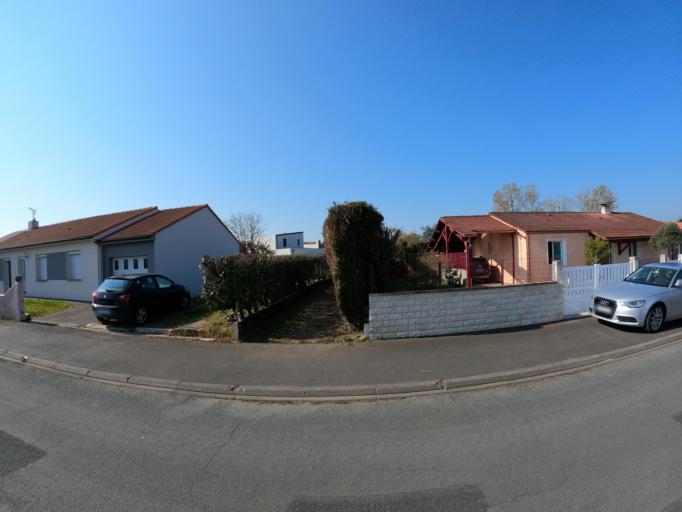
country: FR
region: Pays de la Loire
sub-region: Departement de la Loire-Atlantique
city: Aigrefeuille-sur-Maine
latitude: 47.0819
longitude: -1.4072
